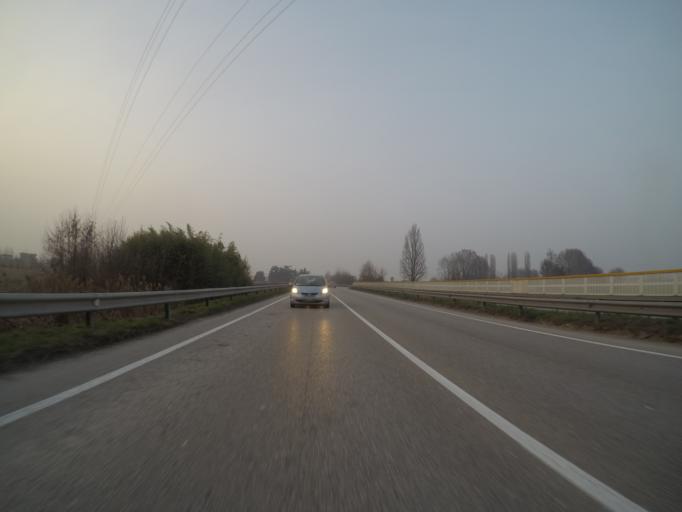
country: IT
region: Veneto
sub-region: Provincia di Padova
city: Cadoneghe
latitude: 45.4500
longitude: 11.9266
